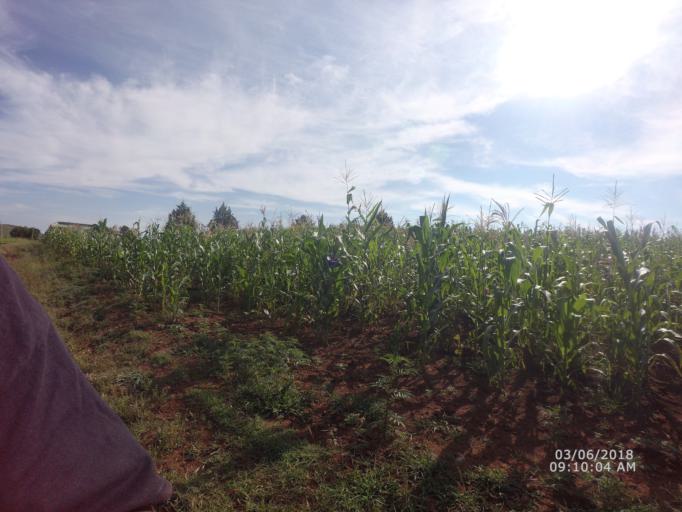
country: LS
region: Berea
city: Teyateyaneng
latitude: -29.2251
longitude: 27.8601
